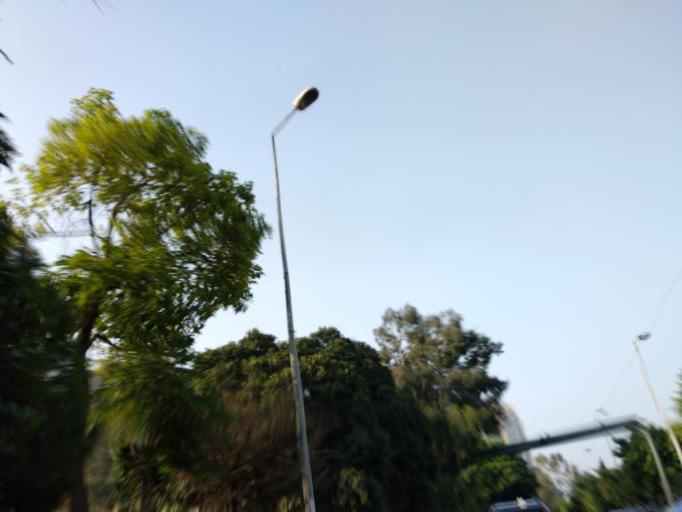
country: LB
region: Beyrouth
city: Beirut
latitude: 33.8832
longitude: 35.5299
